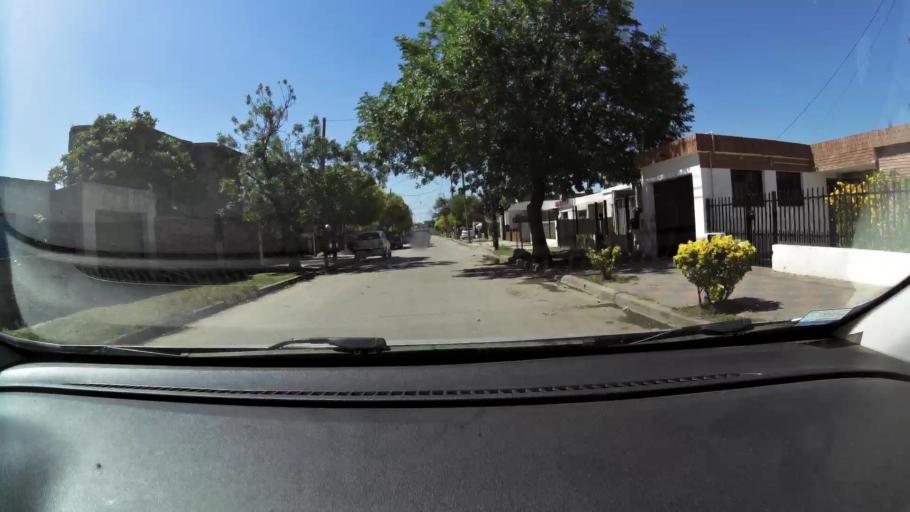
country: AR
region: Cordoba
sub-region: Departamento de Capital
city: Cordoba
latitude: -31.3684
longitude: -64.1430
